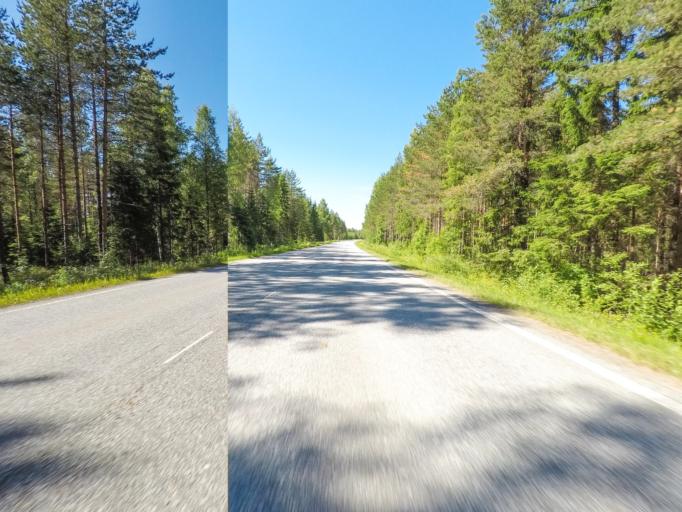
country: FI
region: Southern Savonia
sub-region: Savonlinna
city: Rantasalmi
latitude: 61.9902
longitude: 28.4761
